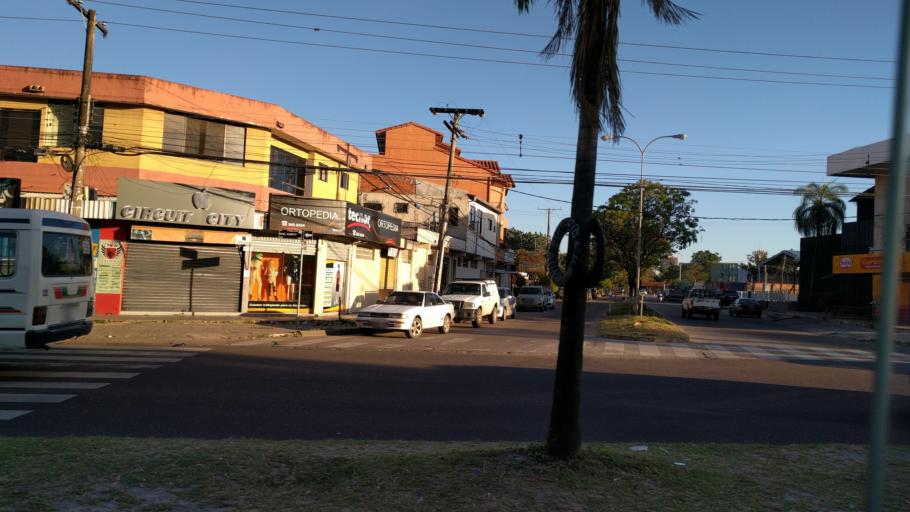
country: BO
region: Santa Cruz
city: Santa Cruz de la Sierra
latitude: -17.7598
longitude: -63.1828
